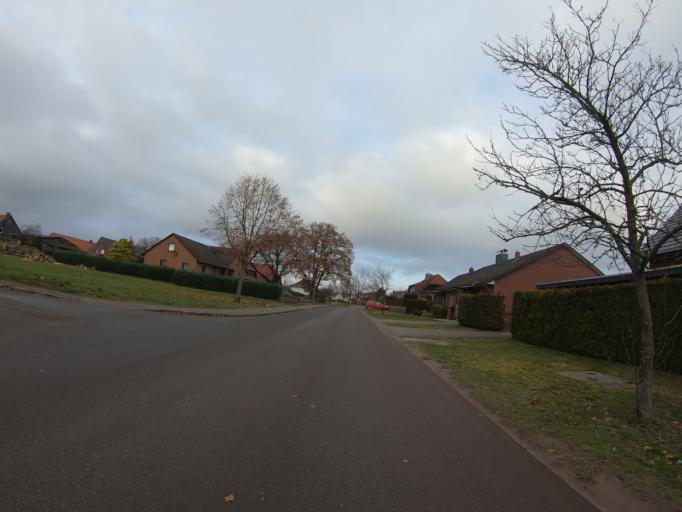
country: DE
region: Lower Saxony
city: Wesendorf
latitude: 52.5845
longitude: 10.5334
